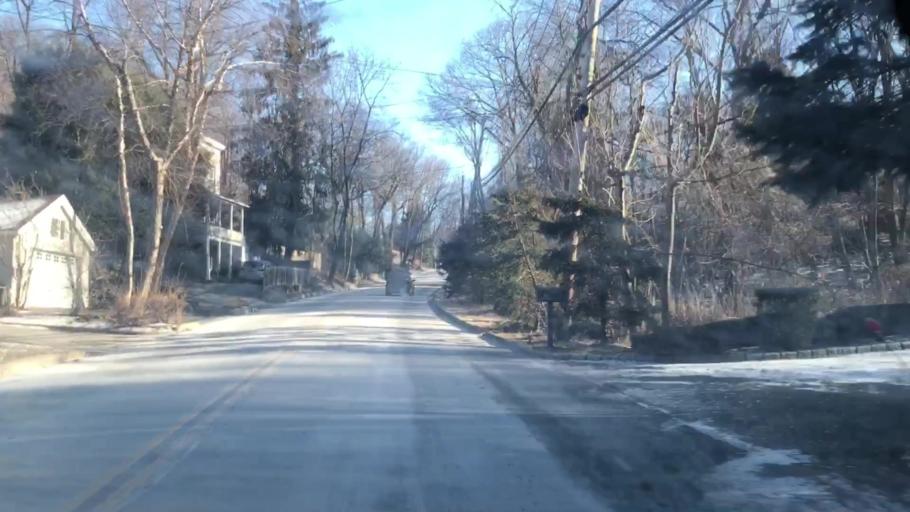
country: US
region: New York
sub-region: Westchester County
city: Greenburgh
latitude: 41.0476
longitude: -73.8421
